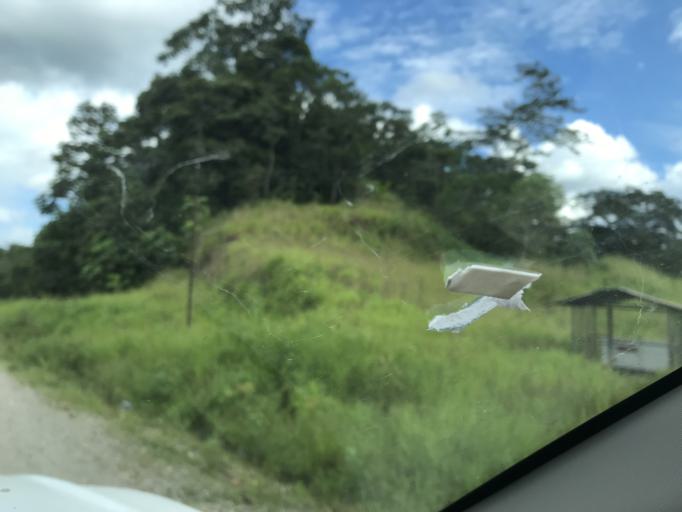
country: EC
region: Orellana
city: Puerto Francisco de Orellana
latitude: -0.6101
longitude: -76.4668
